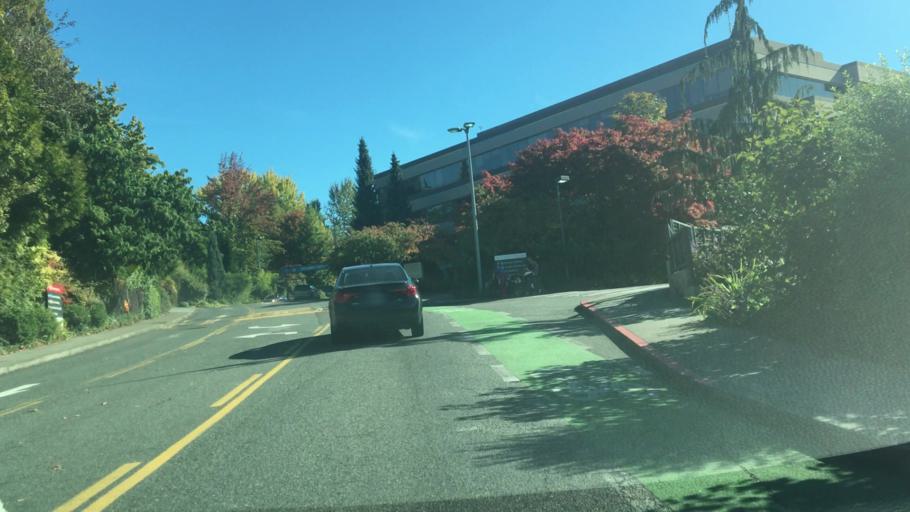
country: US
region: Washington
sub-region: King County
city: Yarrow Point
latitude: 47.6634
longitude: -122.2819
